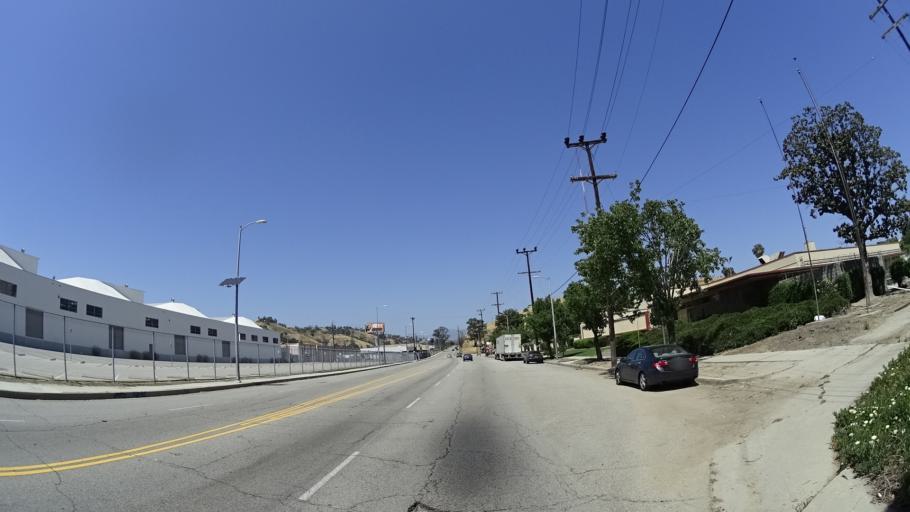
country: US
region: California
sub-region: Los Angeles County
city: Boyle Heights
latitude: 34.0675
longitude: -118.1957
